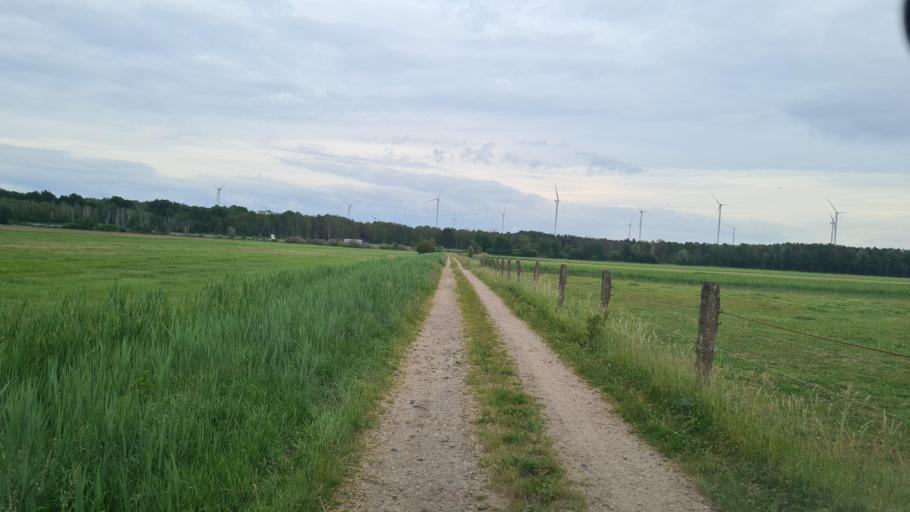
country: DE
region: Brandenburg
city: Bronkow
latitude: 51.6207
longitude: 13.9386
